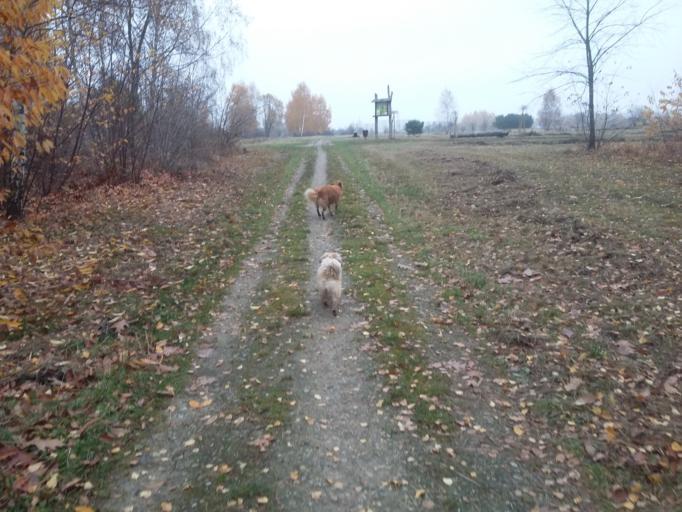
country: PL
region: Lodz Voivodeship
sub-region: Powiat pabianicki
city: Ksawerow
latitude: 51.7300
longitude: 19.3846
